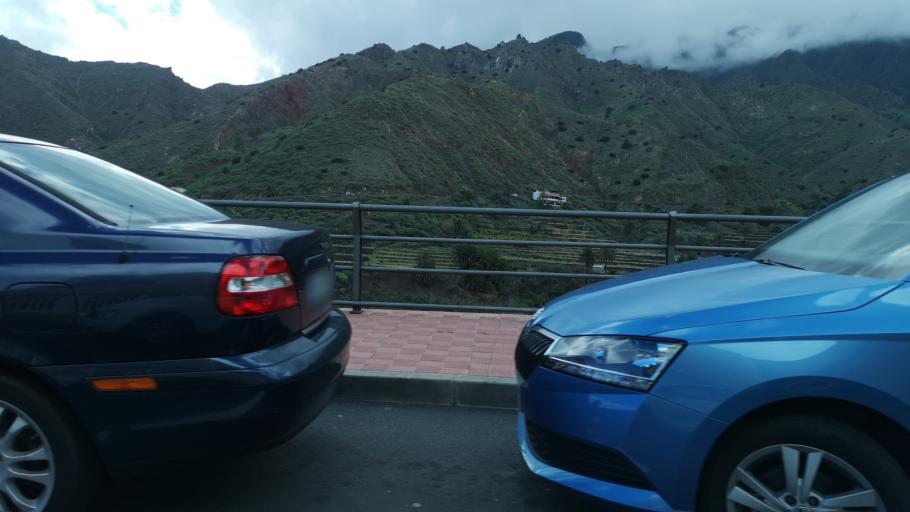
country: ES
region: Canary Islands
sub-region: Provincia de Santa Cruz de Tenerife
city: Hermigua
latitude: 28.1712
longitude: -17.1900
